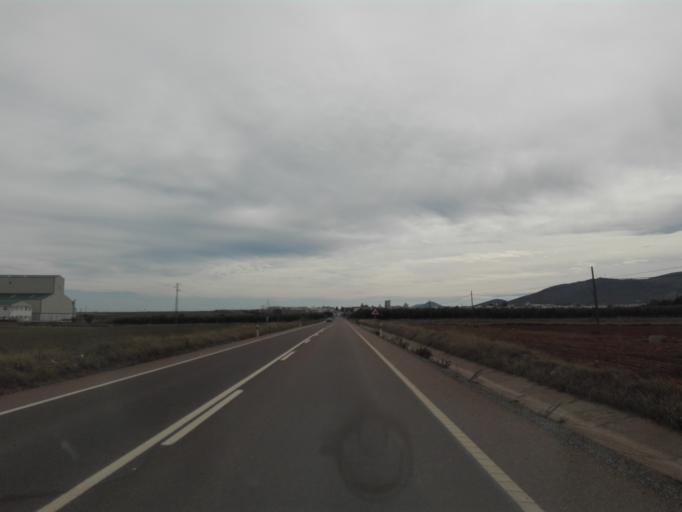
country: ES
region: Extremadura
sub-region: Provincia de Badajoz
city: Llerena
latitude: 38.2521
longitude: -6.0264
